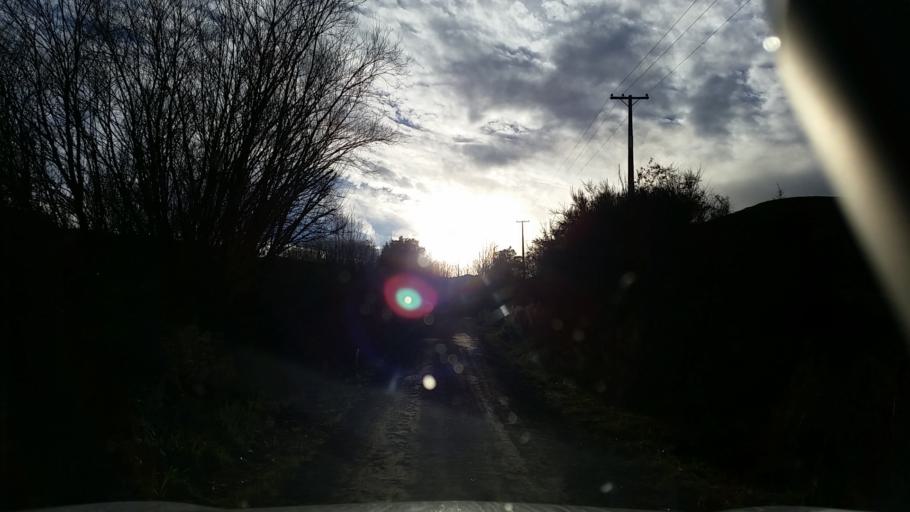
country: NZ
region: Bay of Plenty
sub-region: Rotorua District
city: Rotorua
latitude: -38.2990
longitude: 176.2760
